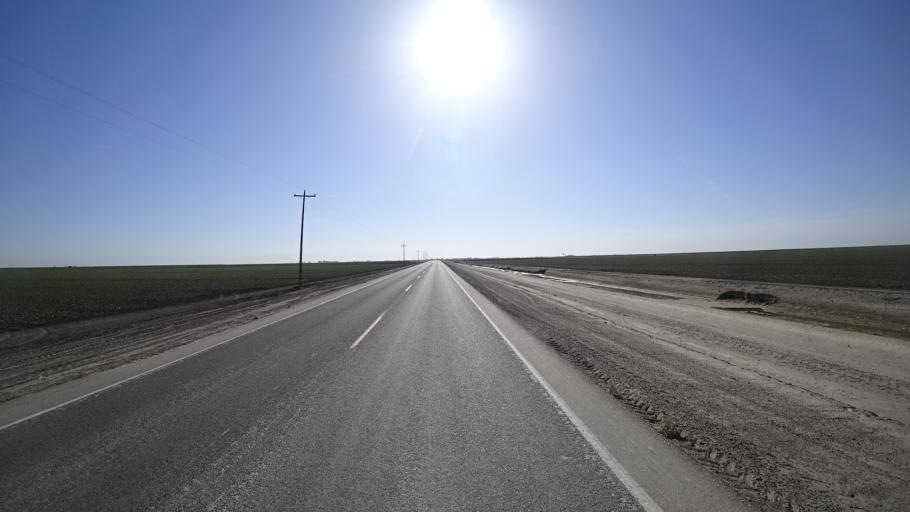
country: US
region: California
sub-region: Kings County
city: Corcoran
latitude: 36.0980
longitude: -119.6404
